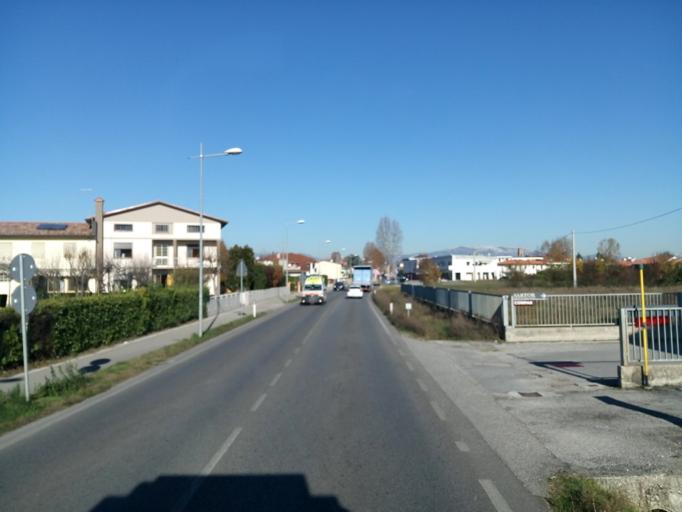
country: IT
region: Veneto
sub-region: Provincia di Treviso
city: Valla
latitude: 45.7019
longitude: 11.9295
